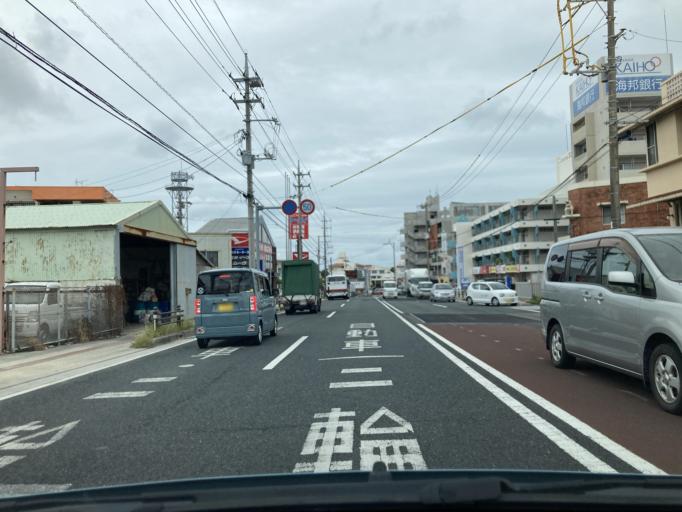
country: JP
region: Okinawa
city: Ginowan
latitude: 26.2001
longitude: 127.7502
